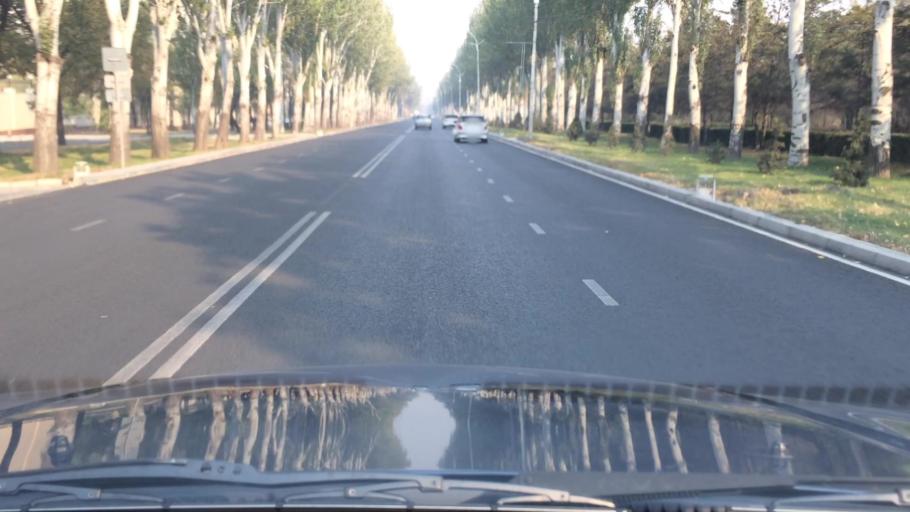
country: KG
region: Chuy
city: Bishkek
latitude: 42.8344
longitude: 74.5855
